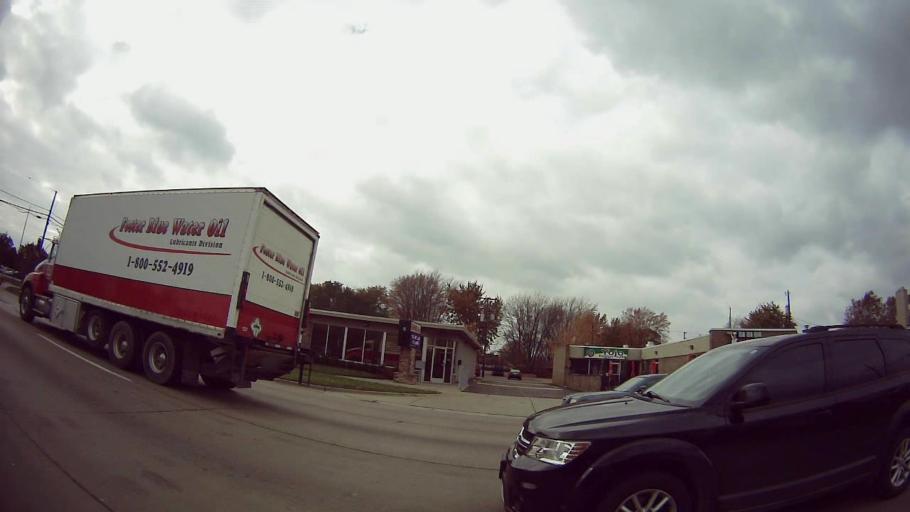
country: US
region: Michigan
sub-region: Macomb County
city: Sterling Heights
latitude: 42.5322
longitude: -83.0480
